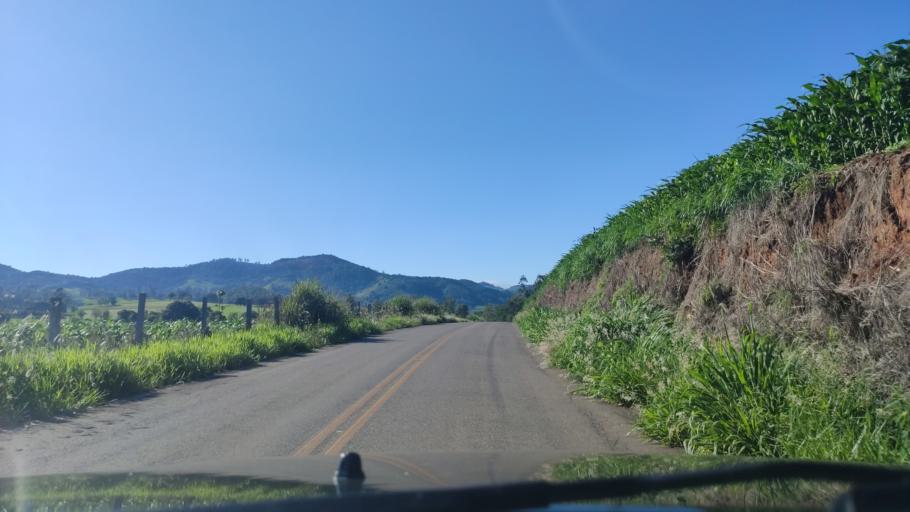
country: BR
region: Sao Paulo
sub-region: Serra Negra
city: Serra Negra
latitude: -22.5705
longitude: -46.6216
